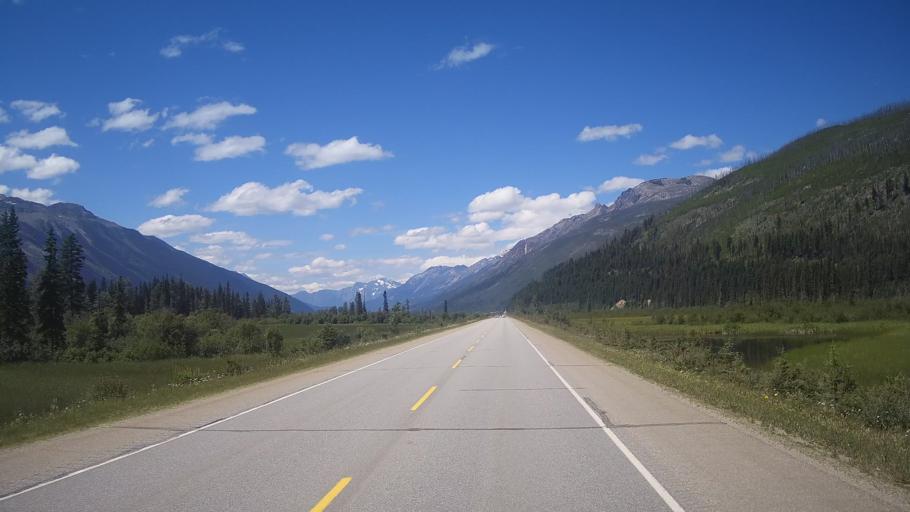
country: CA
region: Alberta
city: Jasper Park Lodge
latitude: 52.9291
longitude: -118.8260
